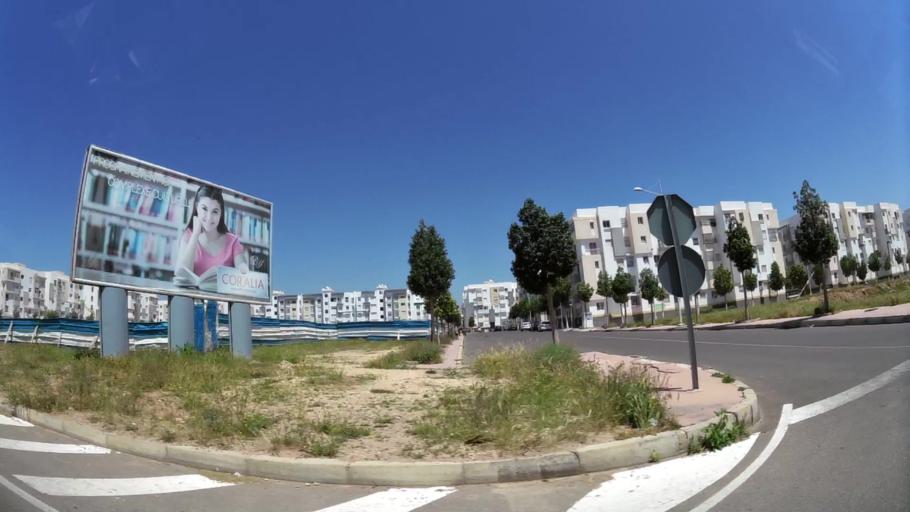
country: MA
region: Oued ed Dahab-Lagouira
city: Dakhla
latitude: 30.4363
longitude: -9.5595
